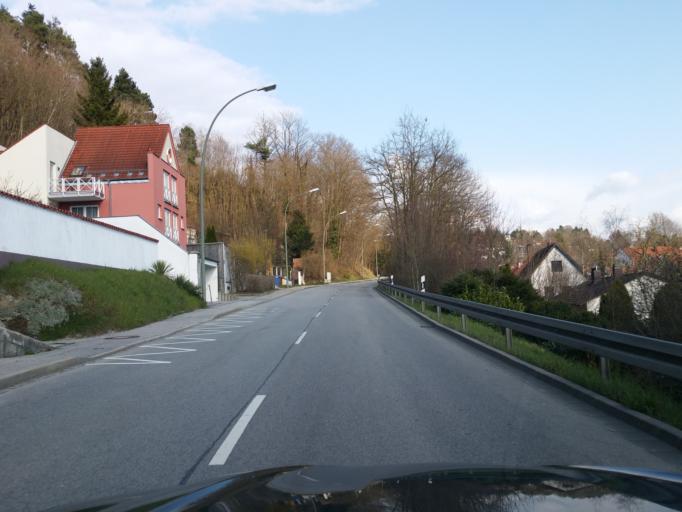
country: DE
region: Bavaria
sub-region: Lower Bavaria
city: Landshut
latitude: 48.5259
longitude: 12.1476
